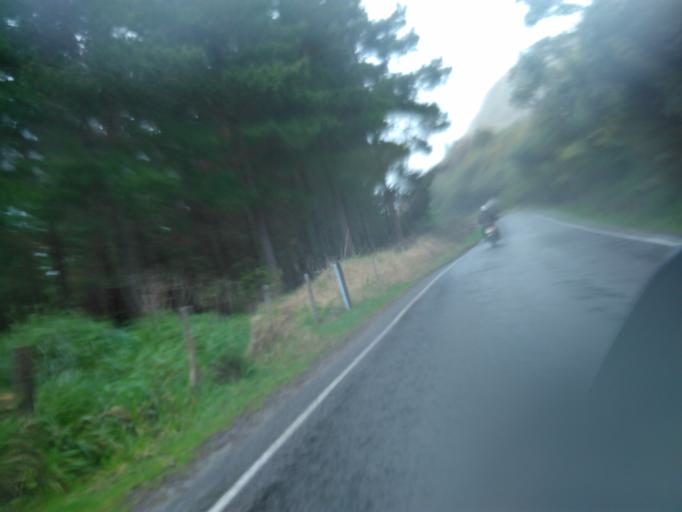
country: NZ
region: Gisborne
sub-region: Gisborne District
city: Gisborne
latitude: -38.6699
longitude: 177.7171
